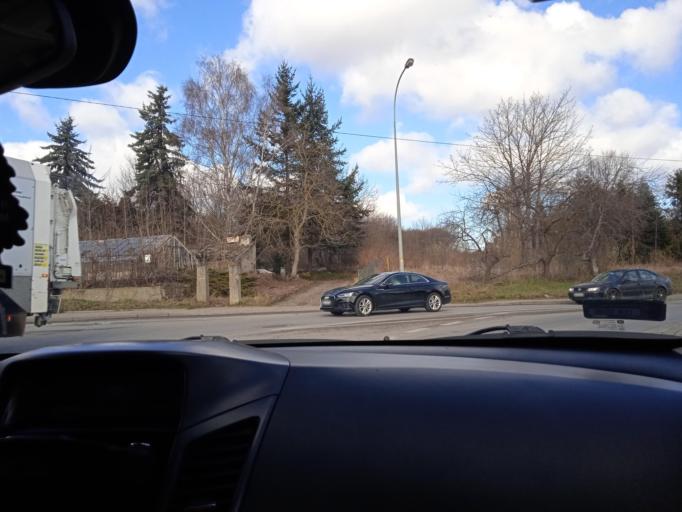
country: PL
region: Pomeranian Voivodeship
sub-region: Powiat gdanski
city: Kowale
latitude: 54.3284
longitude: 18.5519
